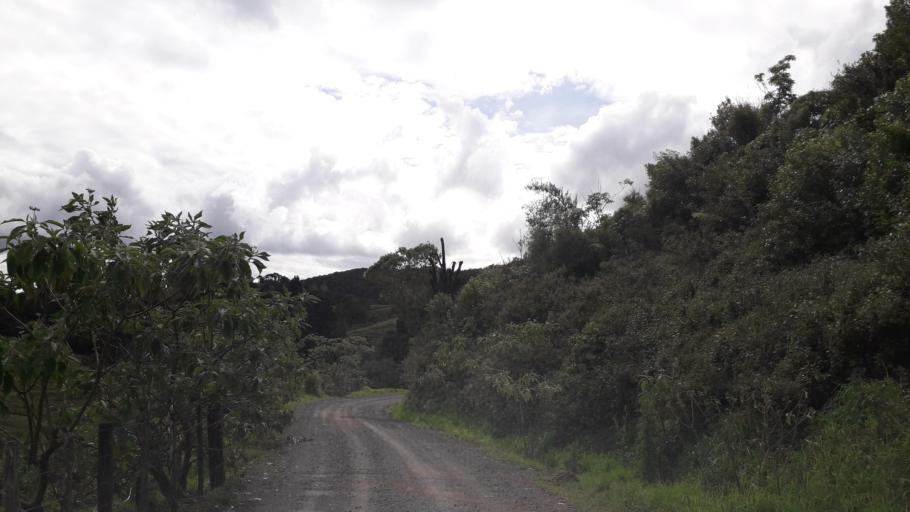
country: NZ
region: Northland
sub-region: Far North District
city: Taipa
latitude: -35.0953
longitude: 173.5380
